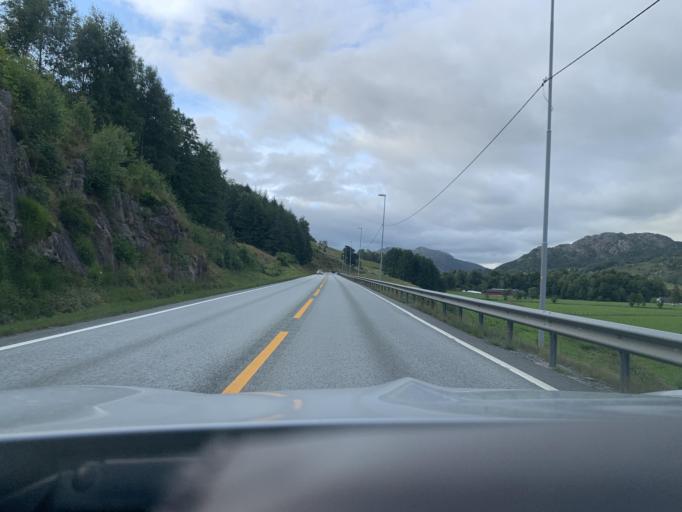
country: NO
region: Rogaland
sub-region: Bjerkreim
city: Vikesa
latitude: 58.6029
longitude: 6.0836
